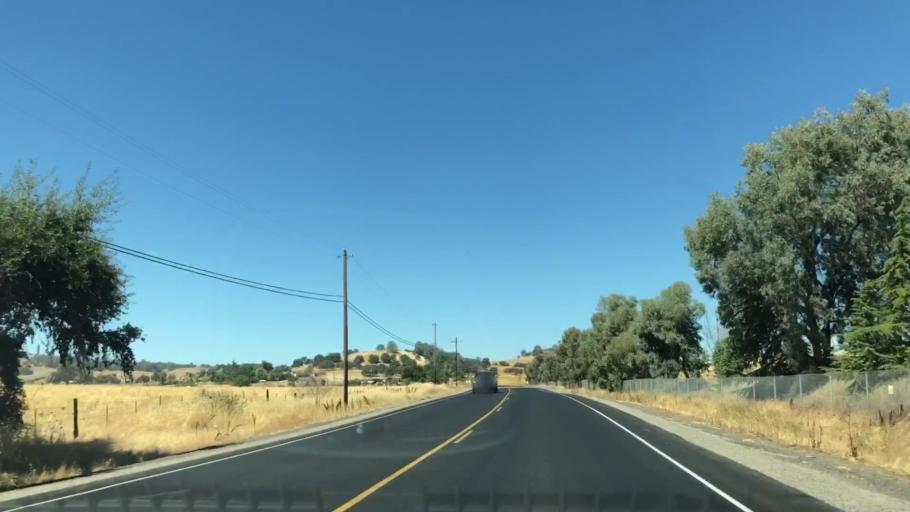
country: US
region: California
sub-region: Tuolumne County
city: Jamestown
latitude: 37.8783
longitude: -120.4506
